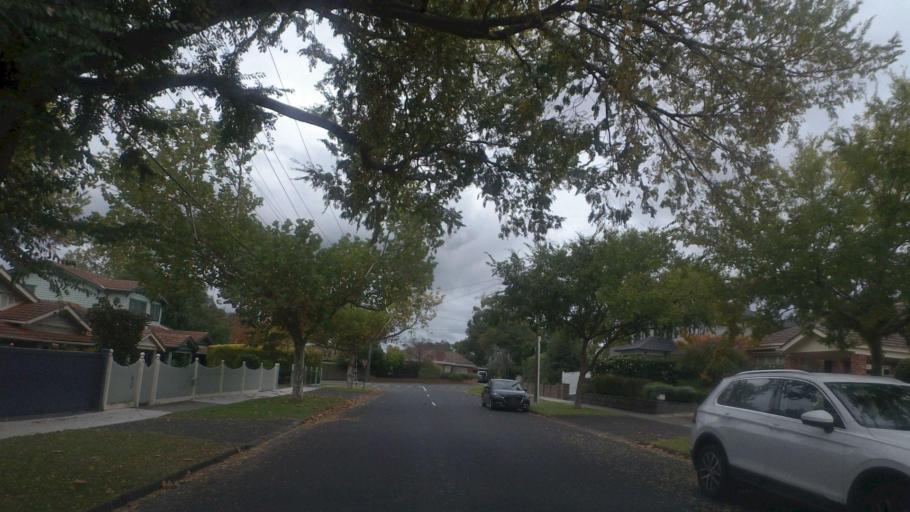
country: AU
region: Victoria
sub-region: Whitehorse
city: Box Hill
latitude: -37.8245
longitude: 145.1317
